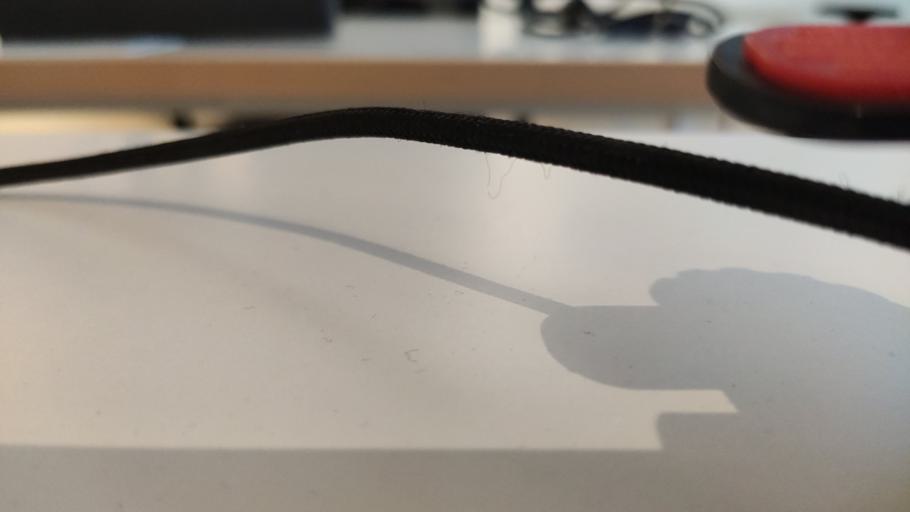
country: RU
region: Moskovskaya
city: Novopetrovskoye
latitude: 55.8719
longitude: 36.4009
